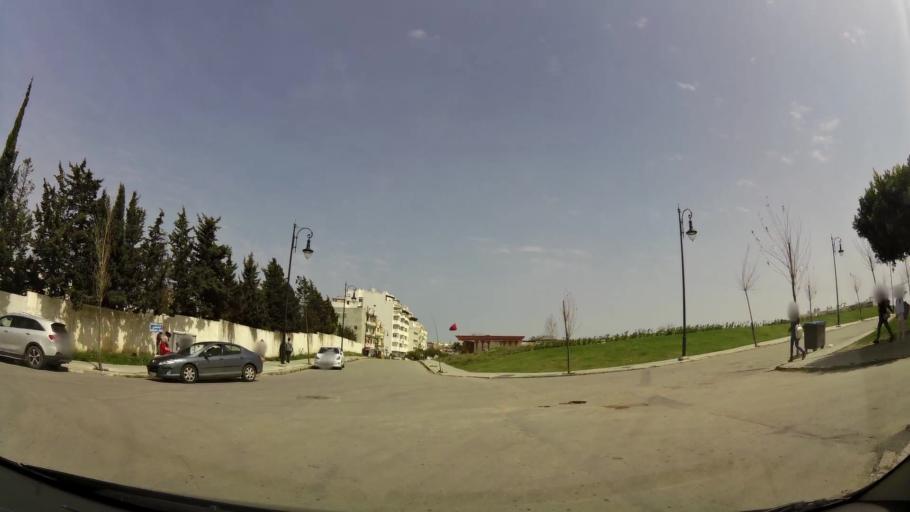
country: MA
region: Tanger-Tetouan
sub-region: Tanger-Assilah
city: Tangier
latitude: 35.7554
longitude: -5.8451
